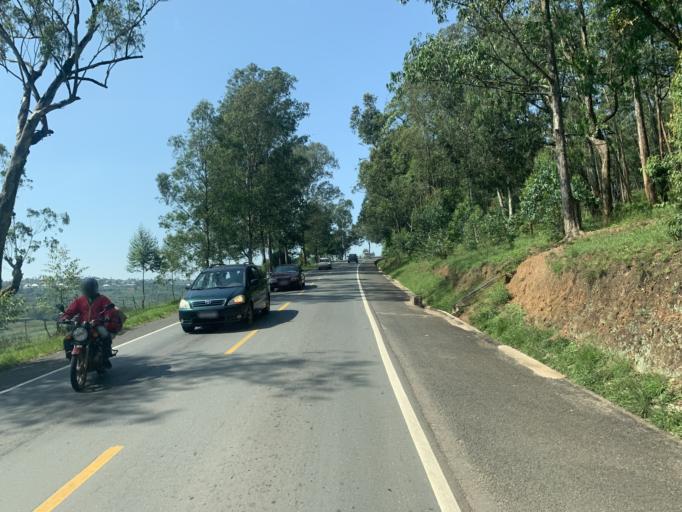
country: RW
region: Kigali
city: Kigali
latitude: -1.9927
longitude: 29.9279
